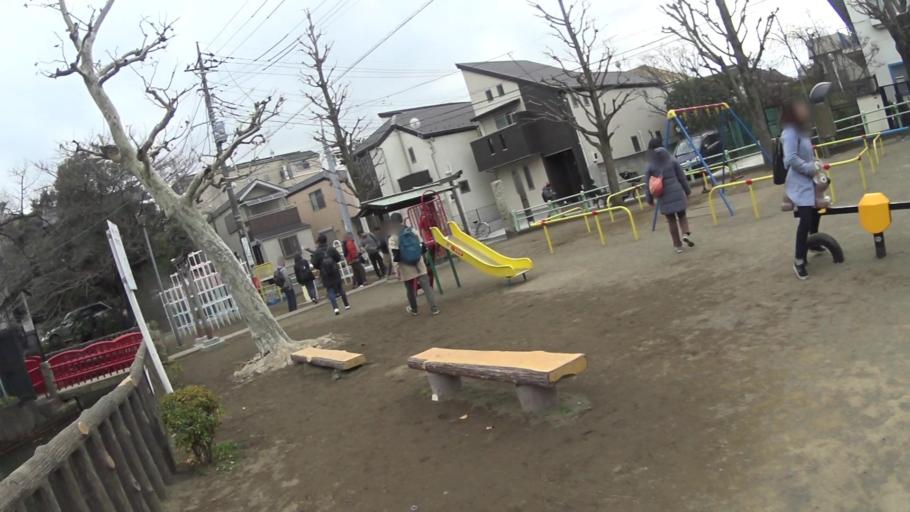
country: JP
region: Kanagawa
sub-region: Kawasaki-shi
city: Kawasaki
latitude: 35.5879
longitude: 139.7209
